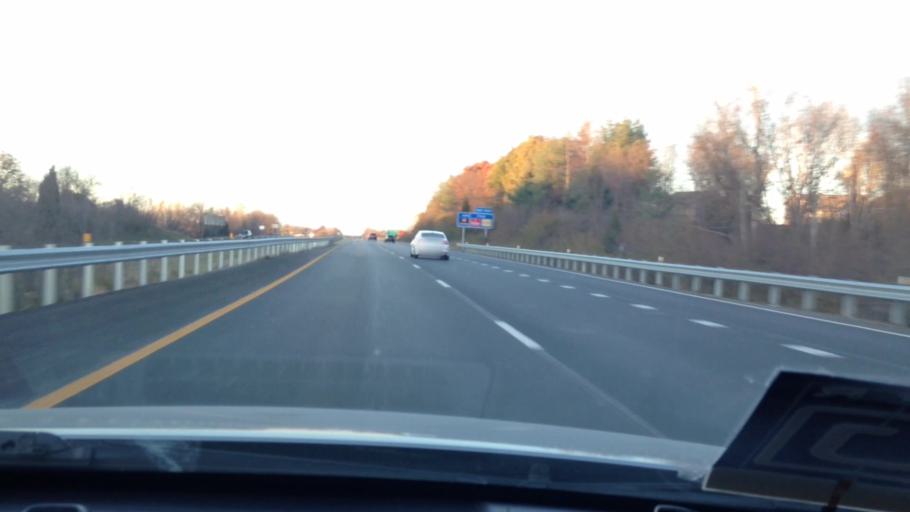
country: US
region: Missouri
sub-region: Platte County
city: Riverside
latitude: 39.1889
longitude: -94.5902
